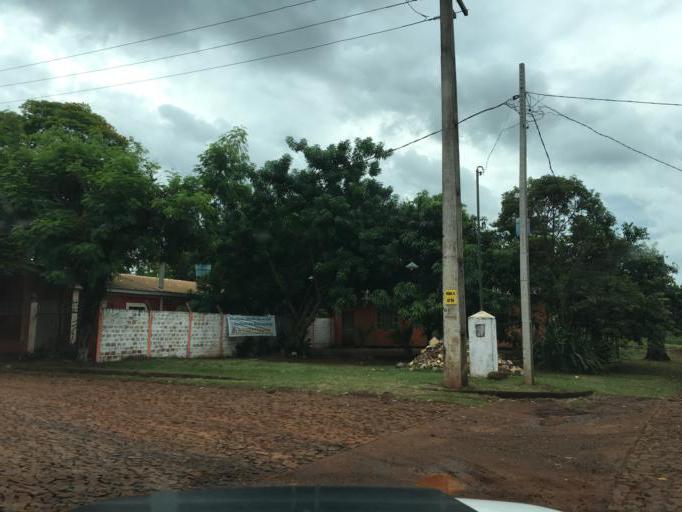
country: PY
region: Alto Parana
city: Ciudad del Este
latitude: -25.4189
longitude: -54.6418
